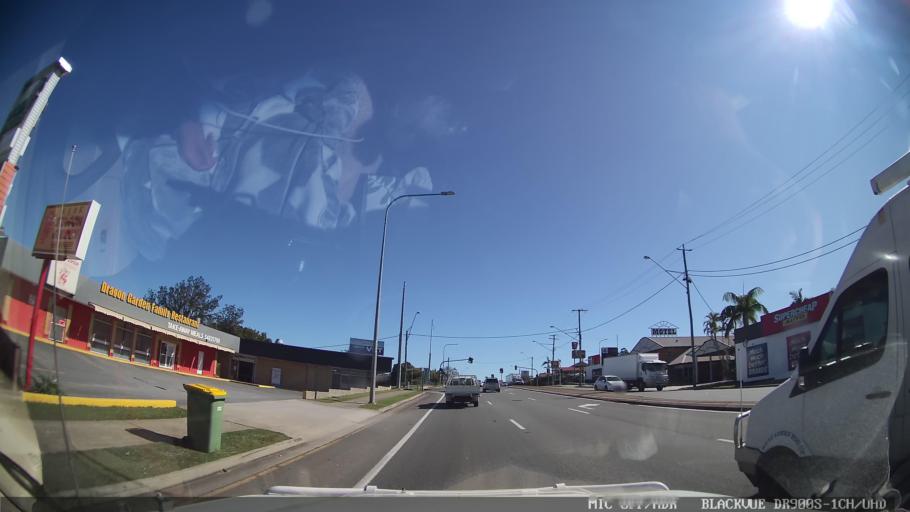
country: AU
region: Queensland
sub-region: Gympie Regional Council
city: Gympie
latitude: -26.1917
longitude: 152.6573
